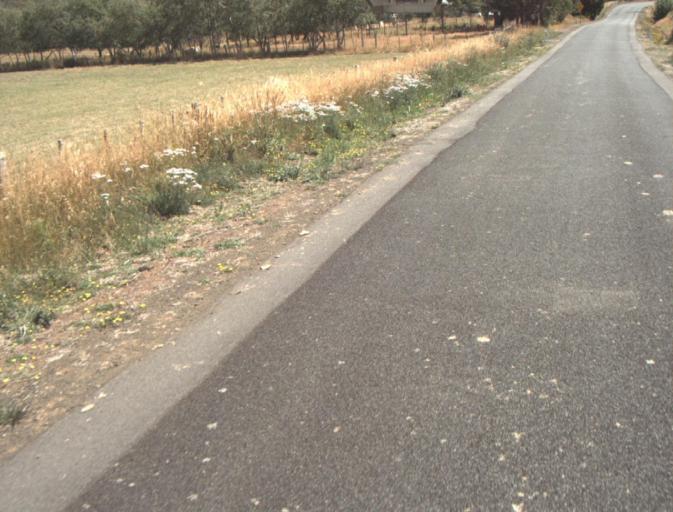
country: AU
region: Tasmania
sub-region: Launceston
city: Newstead
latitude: -41.3417
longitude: 147.3033
